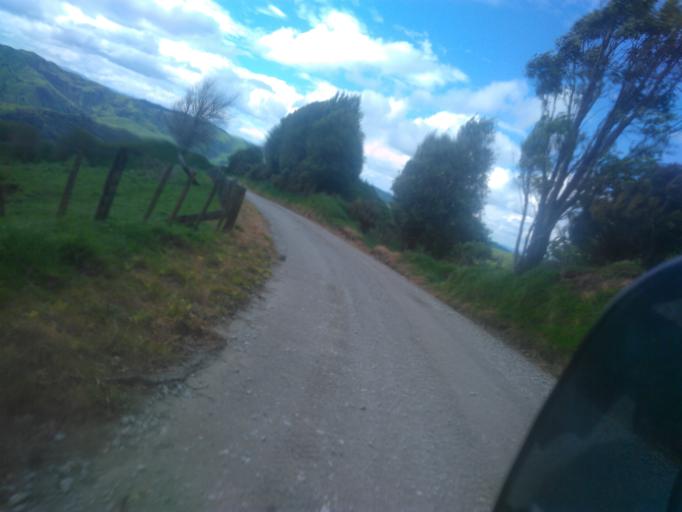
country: NZ
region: Hawke's Bay
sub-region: Wairoa District
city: Wairoa
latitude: -38.7698
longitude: 177.6396
